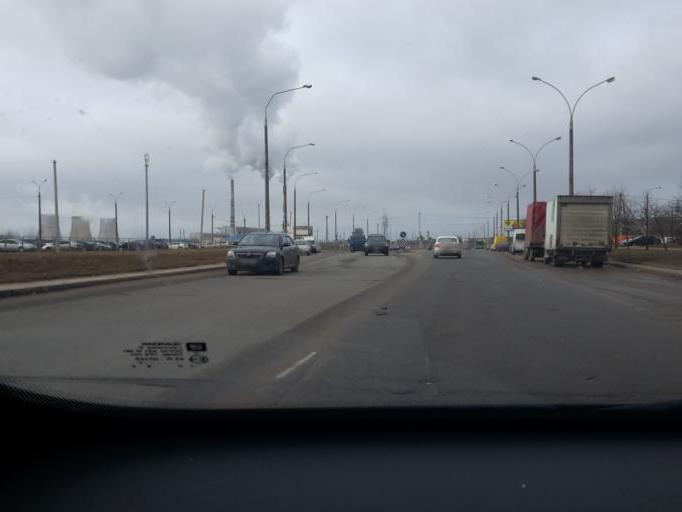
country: BY
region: Minsk
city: Novoye Medvezhino
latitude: 53.8812
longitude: 27.4283
